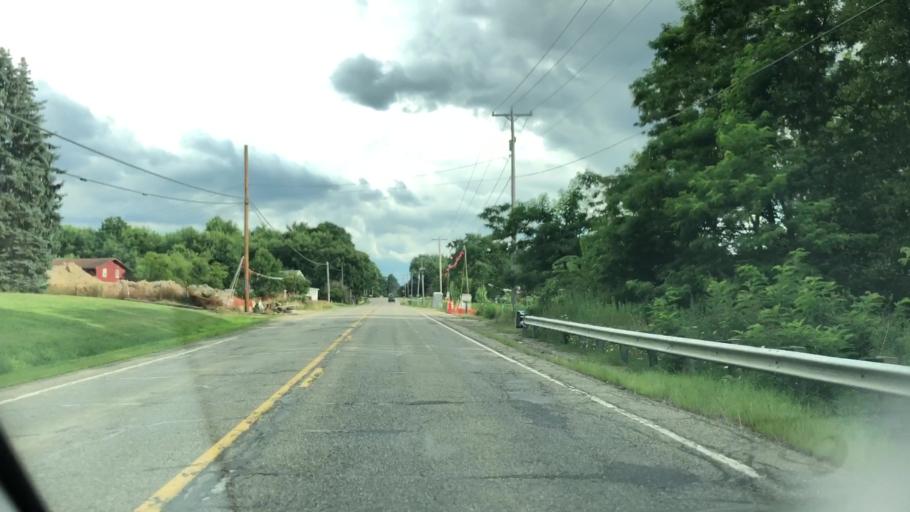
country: US
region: Ohio
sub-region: Summit County
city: Greensburg
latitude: 40.9257
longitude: -81.4644
